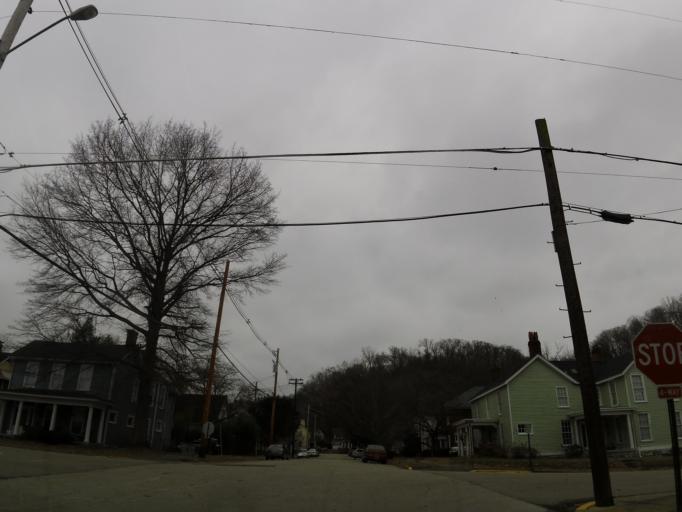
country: US
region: Kentucky
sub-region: Franklin County
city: Frankfort
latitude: 38.1928
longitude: -84.8796
